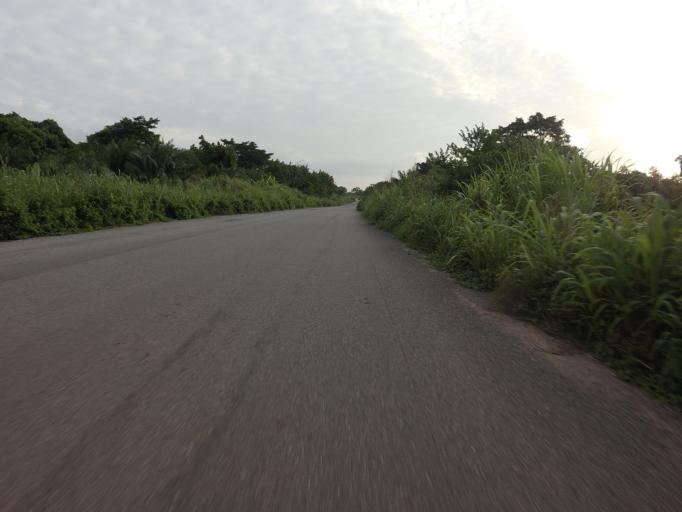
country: GH
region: Volta
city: Kpandu
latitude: 6.8688
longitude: 0.4142
